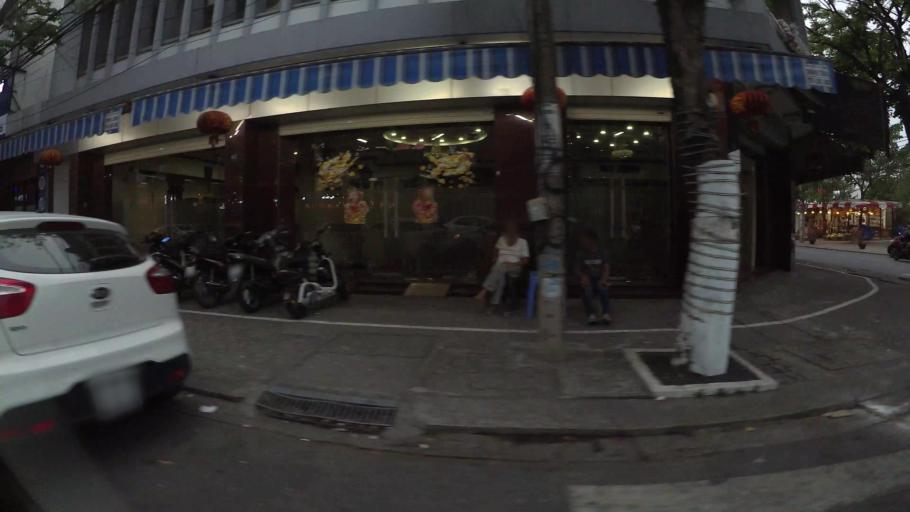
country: VN
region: Da Nang
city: Da Nang
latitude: 16.0685
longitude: 108.2228
